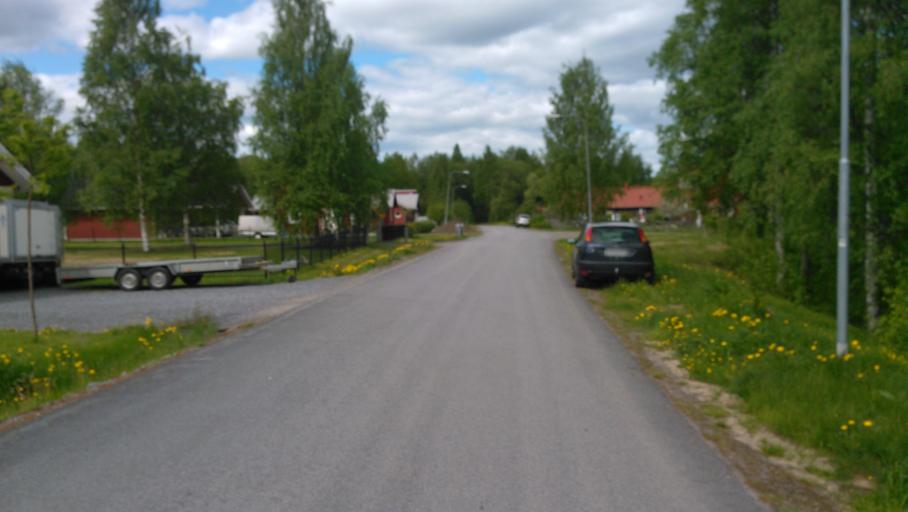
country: SE
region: Vaesterbotten
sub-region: Umea Kommun
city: Roback
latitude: 63.8770
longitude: 20.0534
